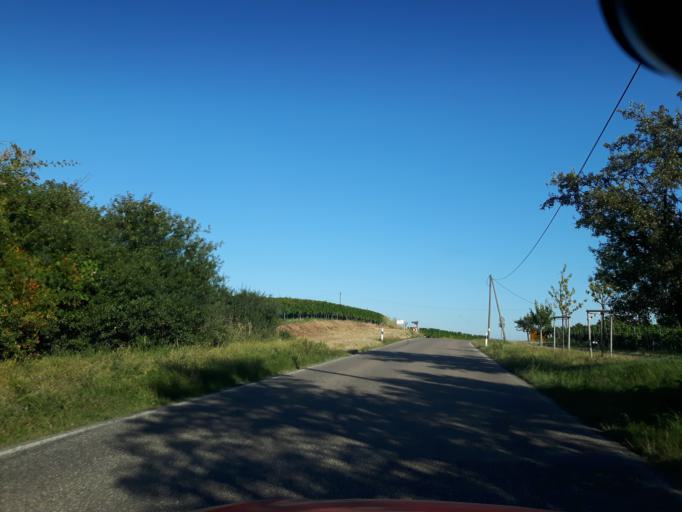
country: DE
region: Baden-Wuerttemberg
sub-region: Regierungsbezirk Stuttgart
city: Cleebronn
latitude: 49.0421
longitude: 9.0523
